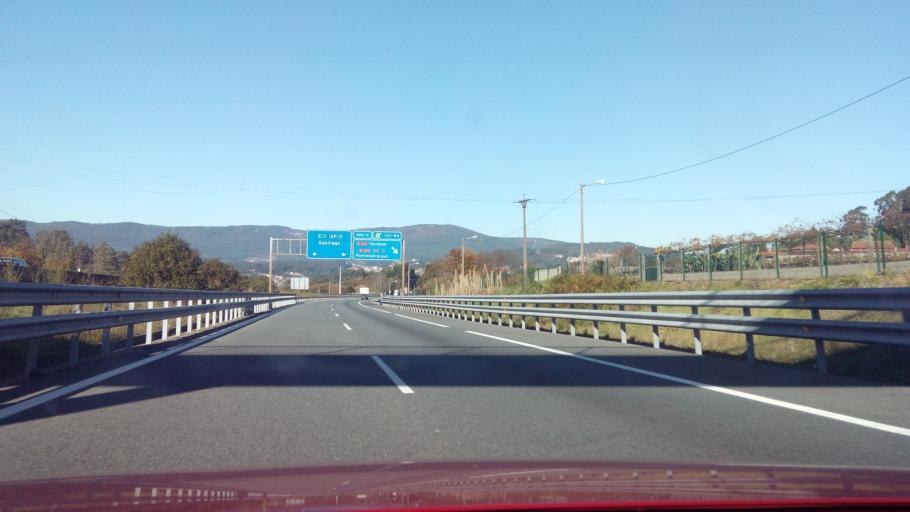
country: ES
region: Galicia
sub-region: Provincia de Pontevedra
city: Poio
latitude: 42.4049
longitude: -8.6510
